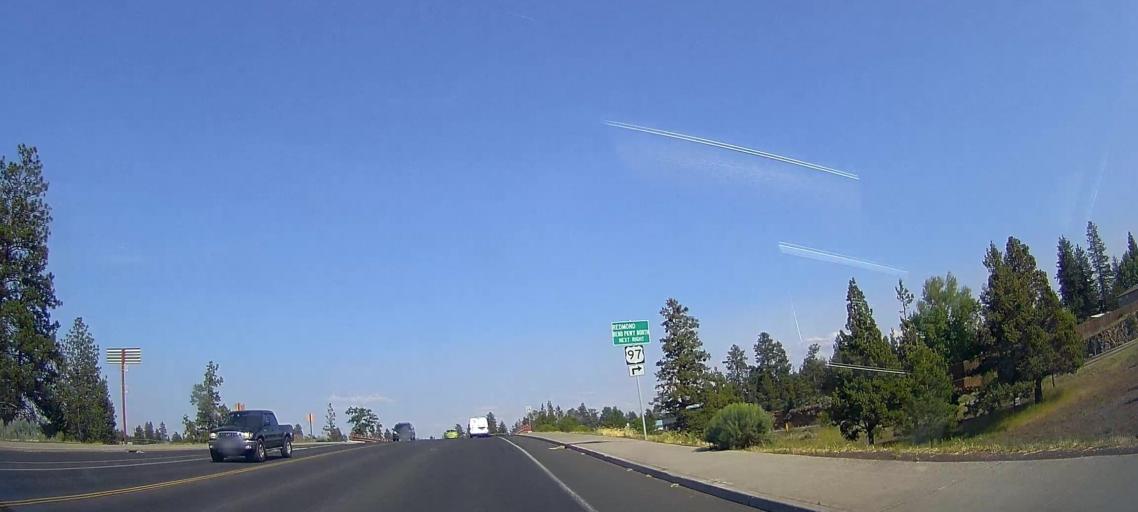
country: US
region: Oregon
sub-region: Deschutes County
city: Bend
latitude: 44.0390
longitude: -121.3097
